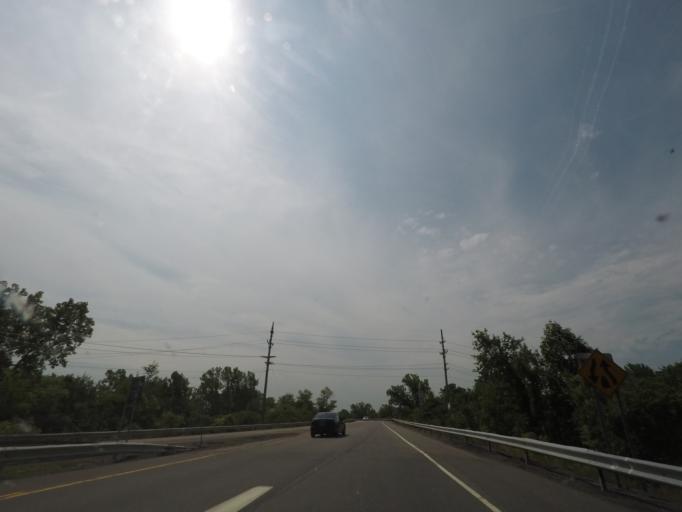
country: US
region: New York
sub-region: Saratoga County
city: Mechanicville
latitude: 42.8875
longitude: -73.6900
